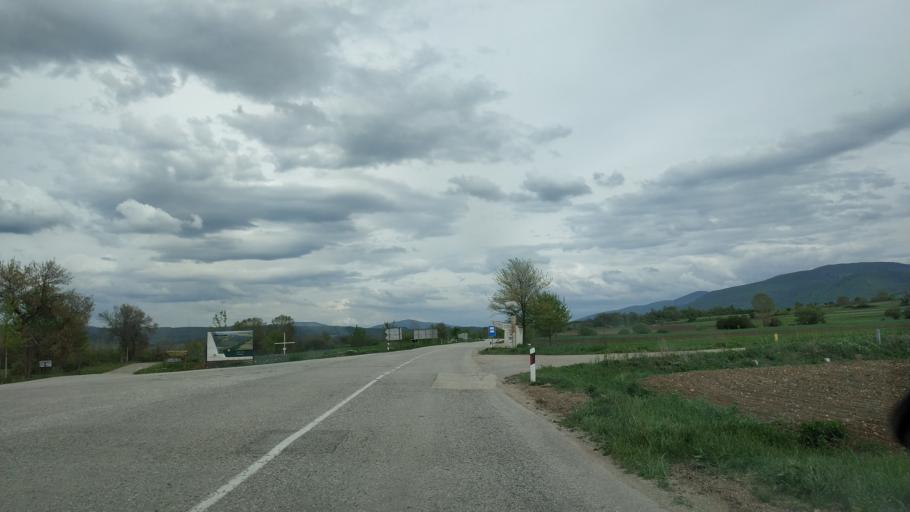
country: RS
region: Central Serbia
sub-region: Zajecarski Okrug
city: Soko Banja
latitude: 43.6568
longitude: 21.8031
